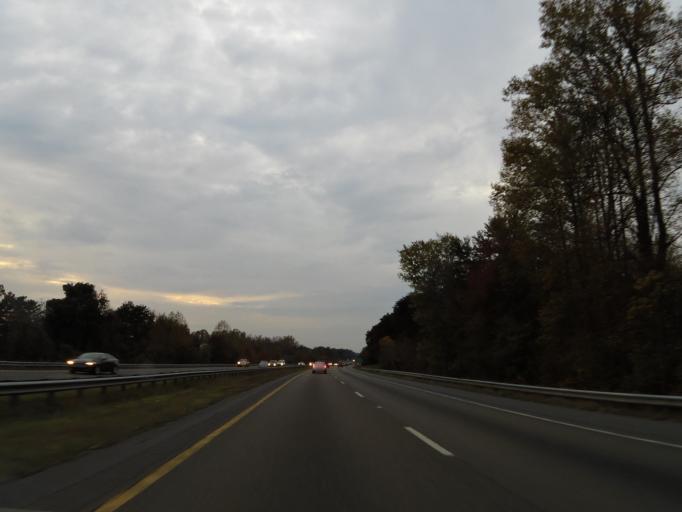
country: US
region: North Carolina
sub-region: Burke County
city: Hildebran
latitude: 35.7062
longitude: -81.4291
